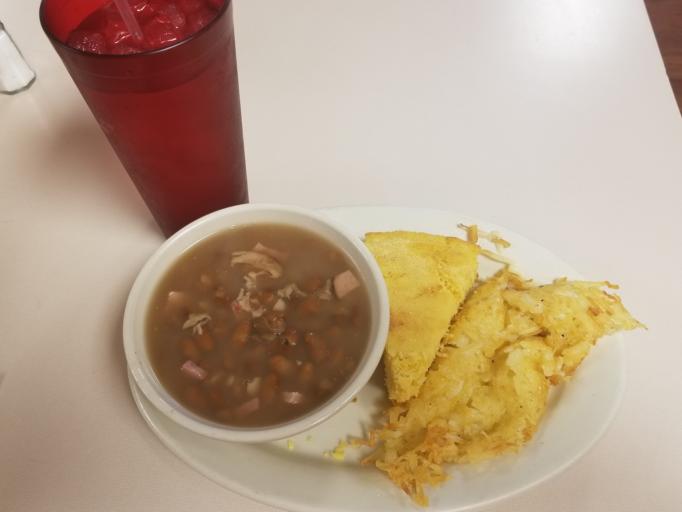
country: US
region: Ohio
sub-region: Scioto County
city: Wheelersburg
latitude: 38.8105
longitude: -82.7205
